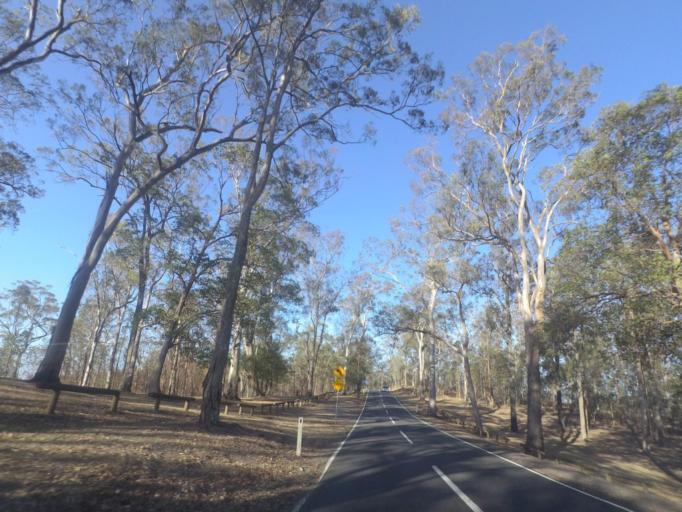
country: AU
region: Queensland
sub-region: Brisbane
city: Kenmore Hills
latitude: -27.4696
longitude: 152.9417
